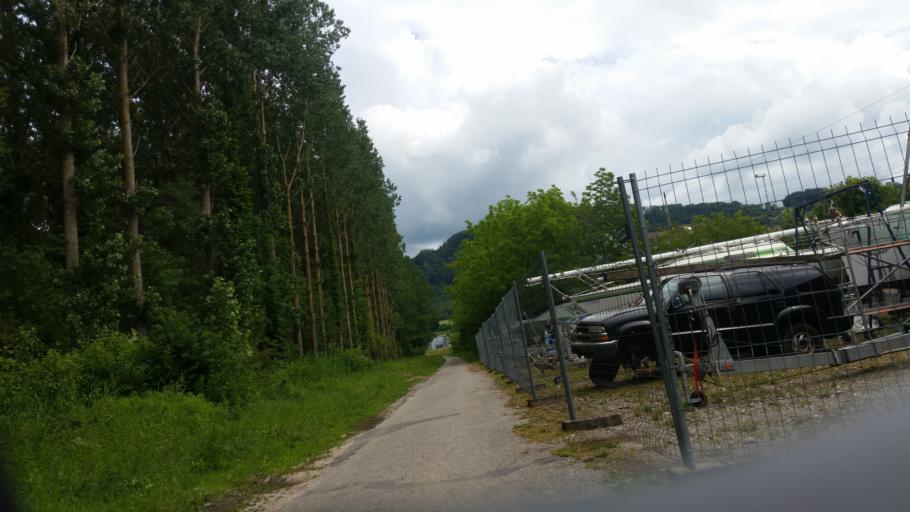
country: CH
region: Vaud
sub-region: Jura-Nord vaudois District
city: Yvonand
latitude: 46.8009
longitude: 6.7489
